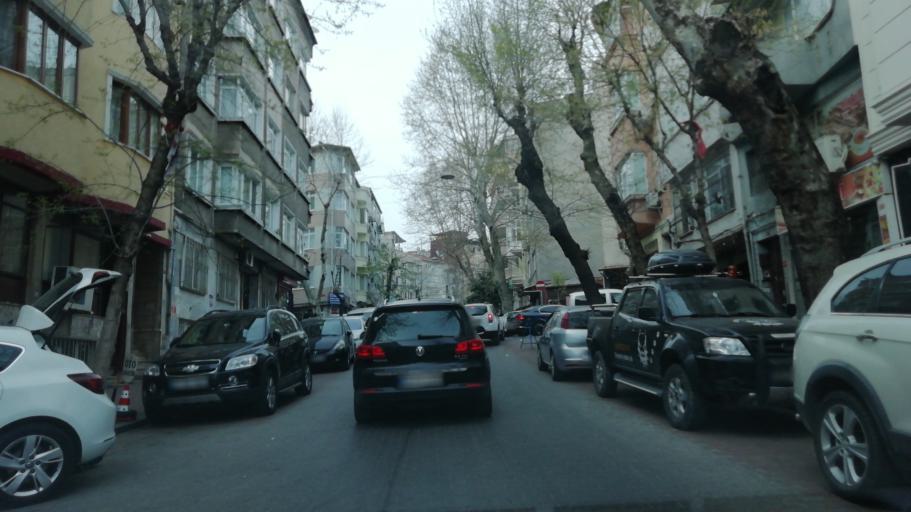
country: TR
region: Istanbul
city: Istanbul
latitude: 41.0154
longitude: 28.9491
